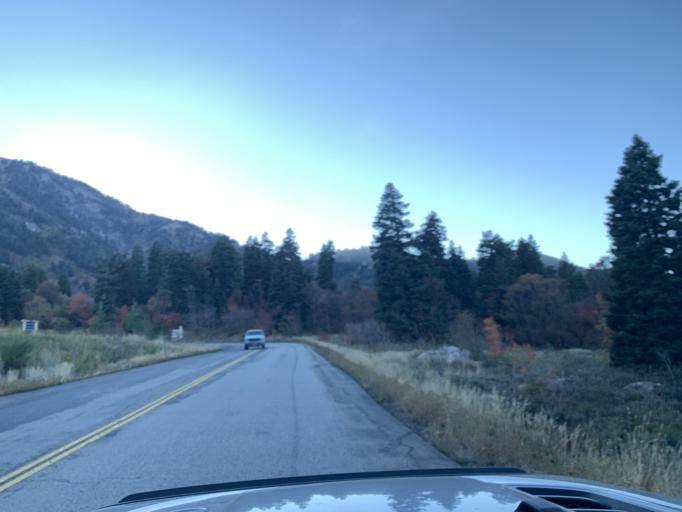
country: US
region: Utah
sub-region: Morgan County
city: Mountain Green
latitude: 41.2191
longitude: -111.8558
